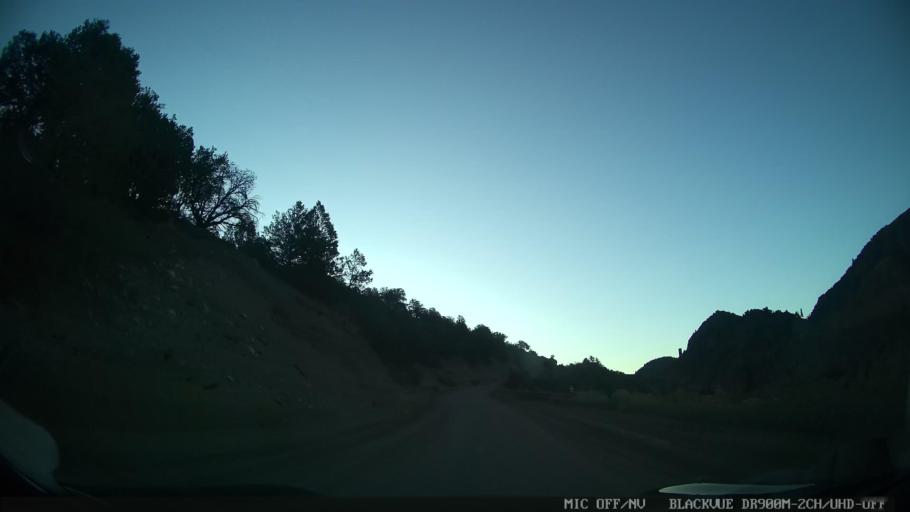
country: US
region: Colorado
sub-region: Eagle County
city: Edwards
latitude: 39.8588
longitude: -106.6477
